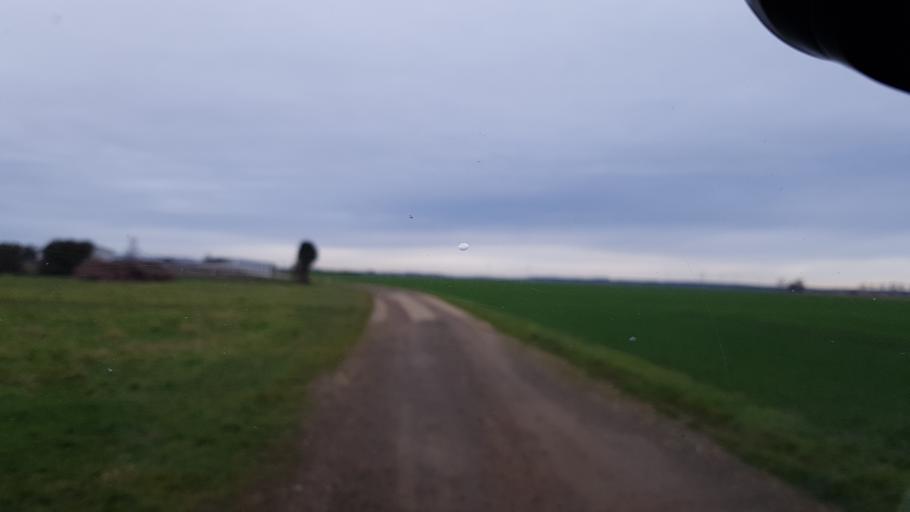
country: DE
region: Brandenburg
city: Doberlug-Kirchhain
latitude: 51.6529
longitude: 13.5481
